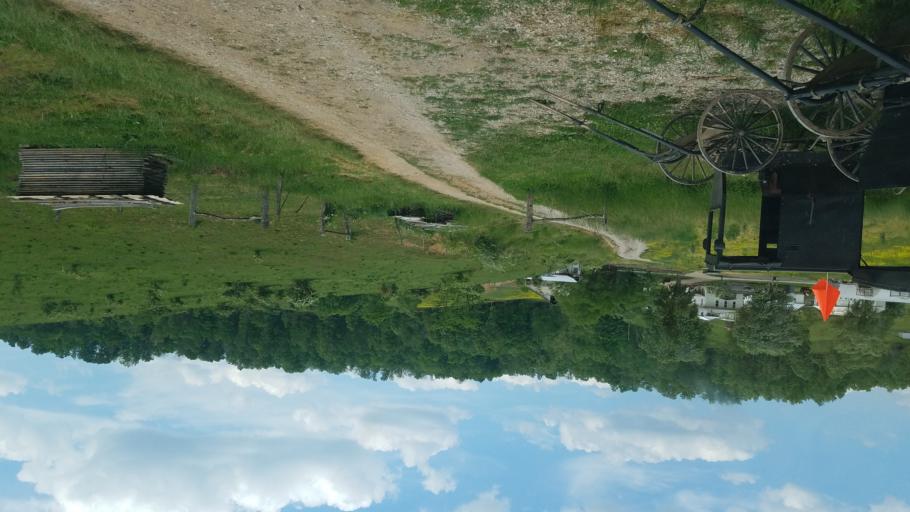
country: US
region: Ohio
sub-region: Meigs County
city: Pomeroy
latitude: 39.1194
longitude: -82.1521
